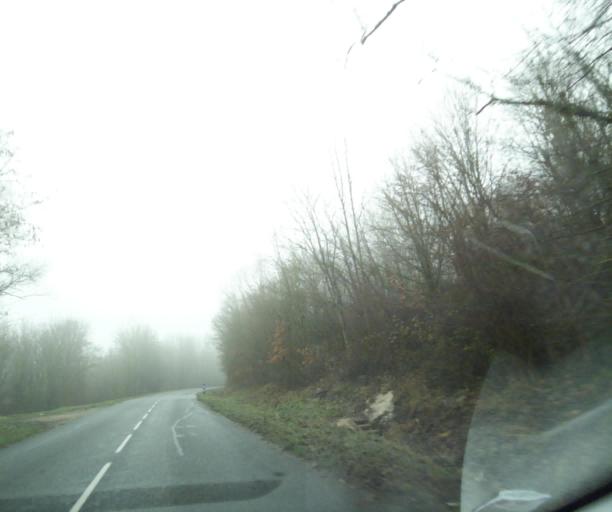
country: FR
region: Ile-de-France
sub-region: Departement de Seine-et-Marne
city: Saint-Mard
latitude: 49.0446
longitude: 2.6885
